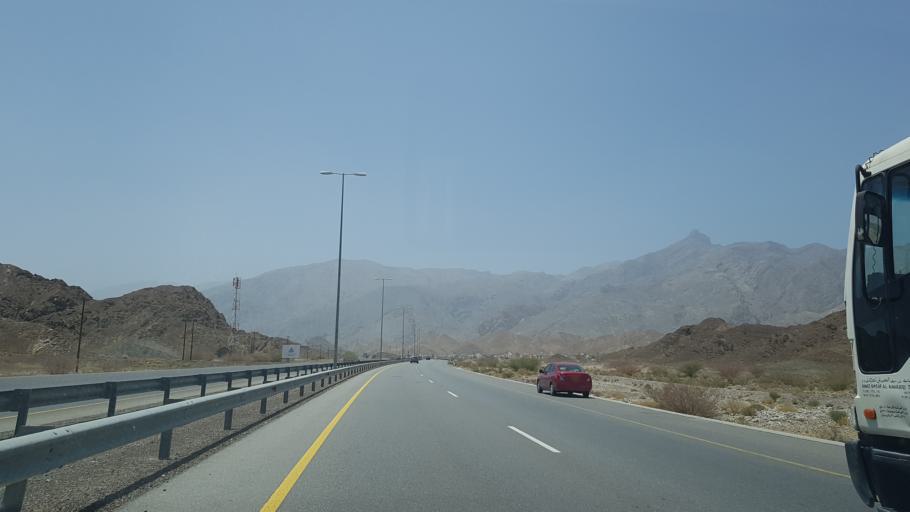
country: OM
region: Muhafazat ad Dakhiliyah
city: Sufalat Sama'il
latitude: 23.3273
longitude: 57.9723
